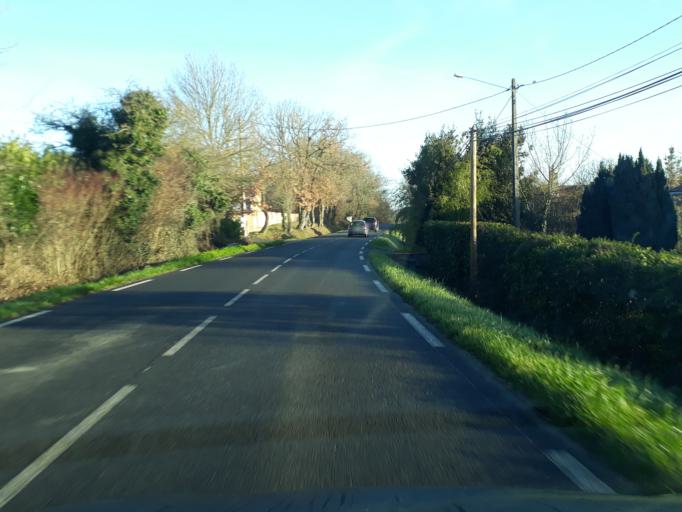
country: FR
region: Midi-Pyrenees
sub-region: Departement de la Haute-Garonne
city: Sainte-Foy-de-Peyrolieres
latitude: 43.4855
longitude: 1.1465
